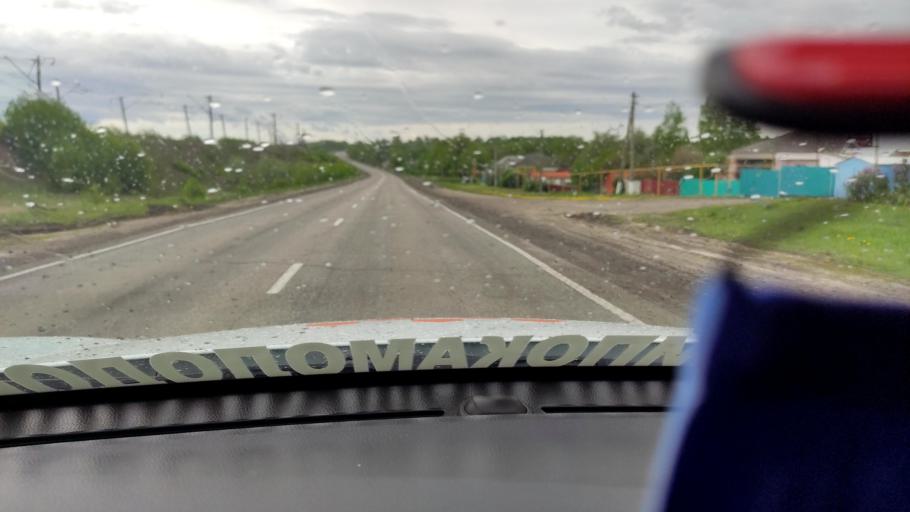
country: RU
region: Voronezj
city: Imeni Pervogo Maya
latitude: 50.7587
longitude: 39.3894
